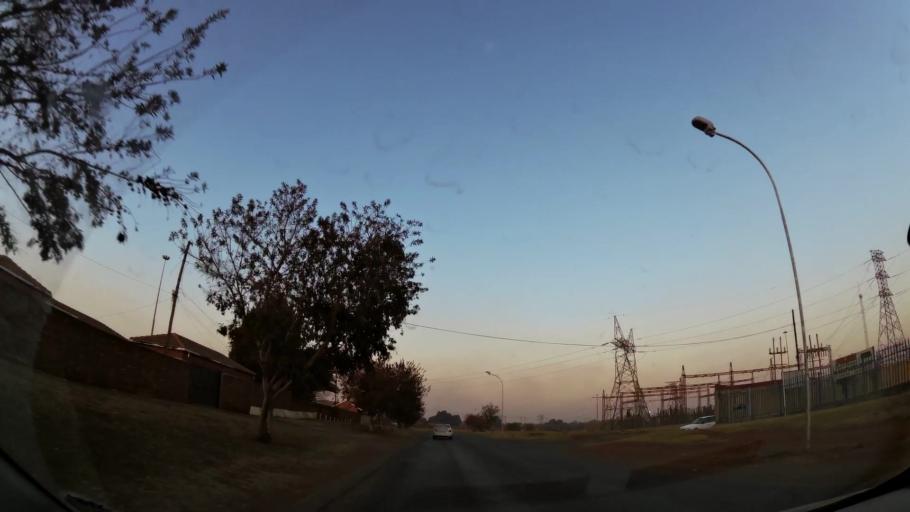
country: ZA
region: Gauteng
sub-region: Ekurhuleni Metropolitan Municipality
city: Springs
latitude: -26.3032
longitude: 28.4117
